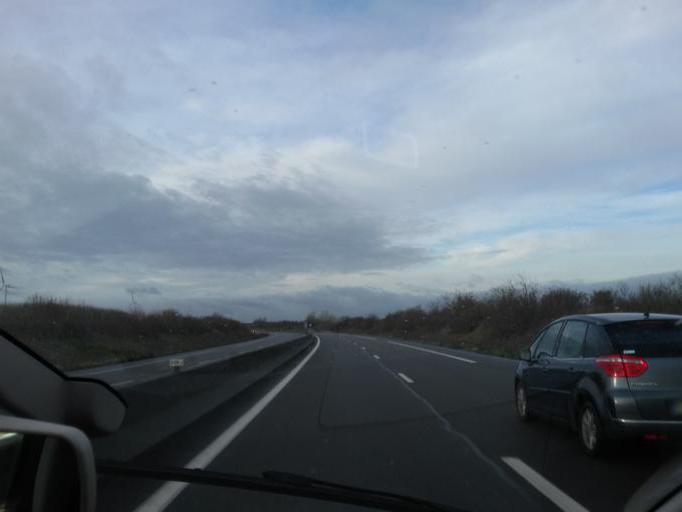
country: FR
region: Picardie
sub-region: Departement de la Somme
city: Chaulnes
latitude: 49.8581
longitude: 2.7790
